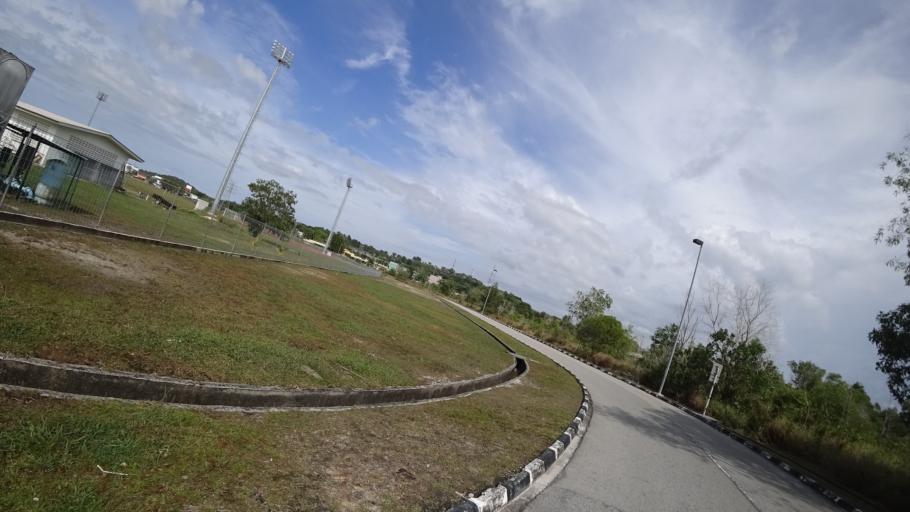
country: BN
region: Tutong
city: Tutong
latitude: 4.8121
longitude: 114.6585
